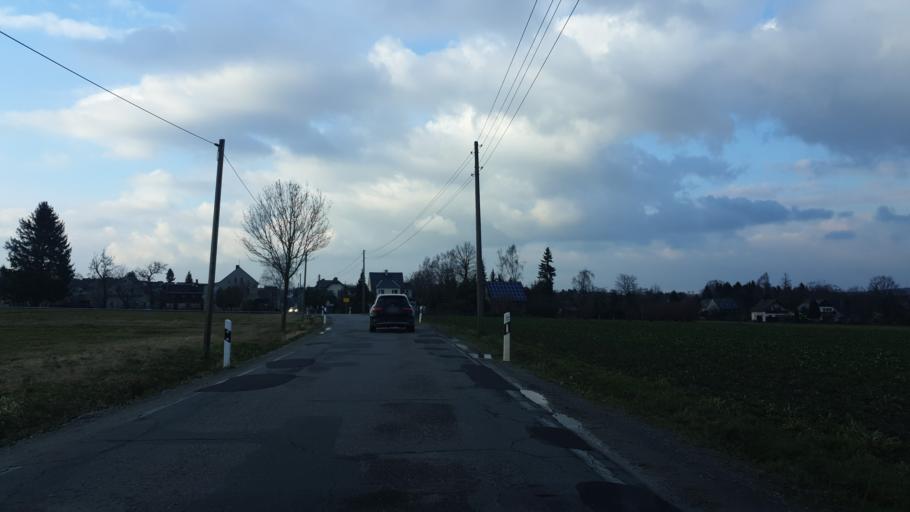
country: DE
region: Saxony
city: Niederdorf
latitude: 50.7614
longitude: 12.8045
